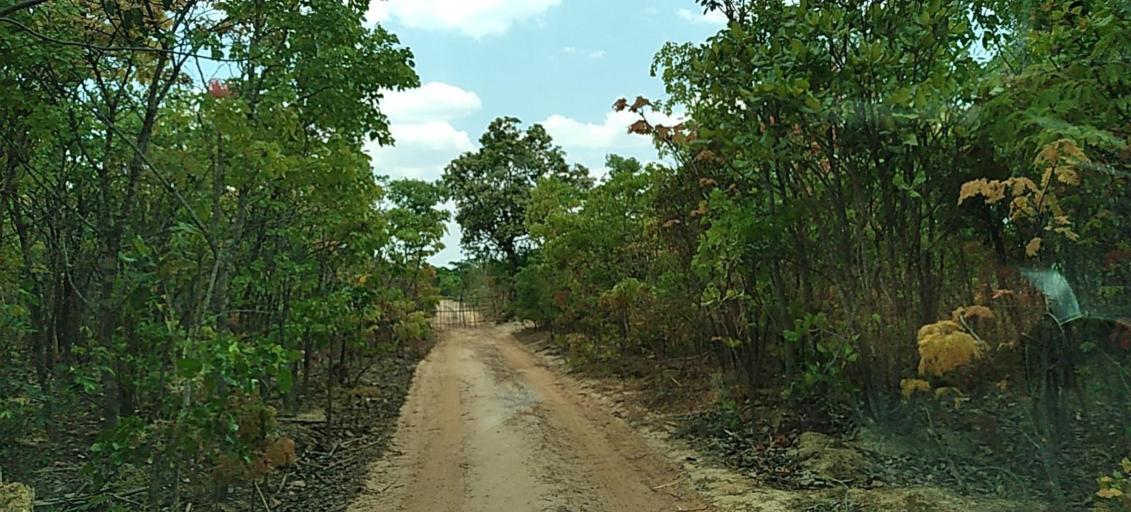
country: ZM
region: Copperbelt
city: Chililabombwe
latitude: -12.4820
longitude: 27.7009
